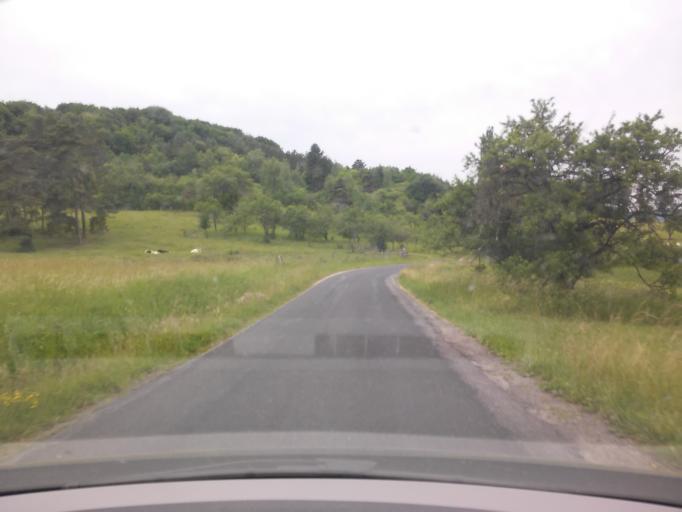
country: FR
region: Lorraine
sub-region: Departement de la Meuse
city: Vignot
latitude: 48.8000
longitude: 5.6616
